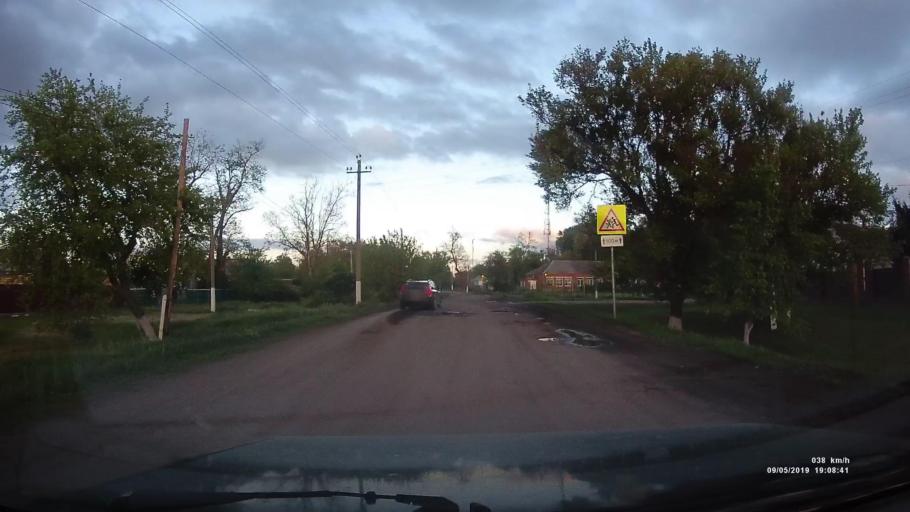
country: RU
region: Krasnodarskiy
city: Kanelovskaya
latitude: 46.7286
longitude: 39.2058
